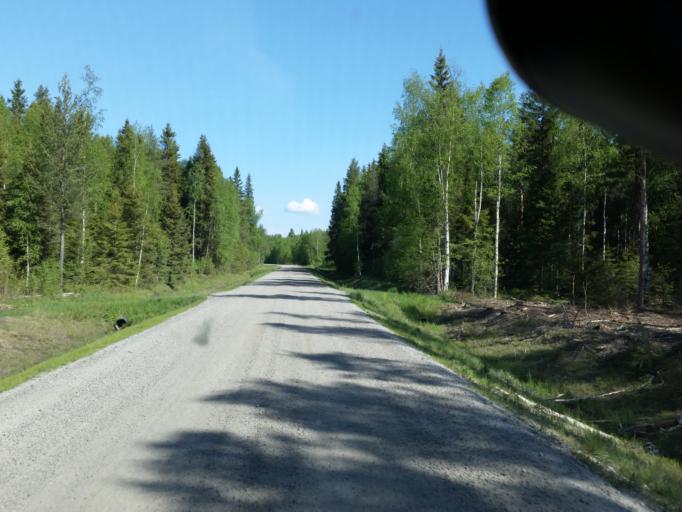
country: SE
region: Norrbotten
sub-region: Pitea Kommun
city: Roknas
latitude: 65.4112
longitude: 21.2399
